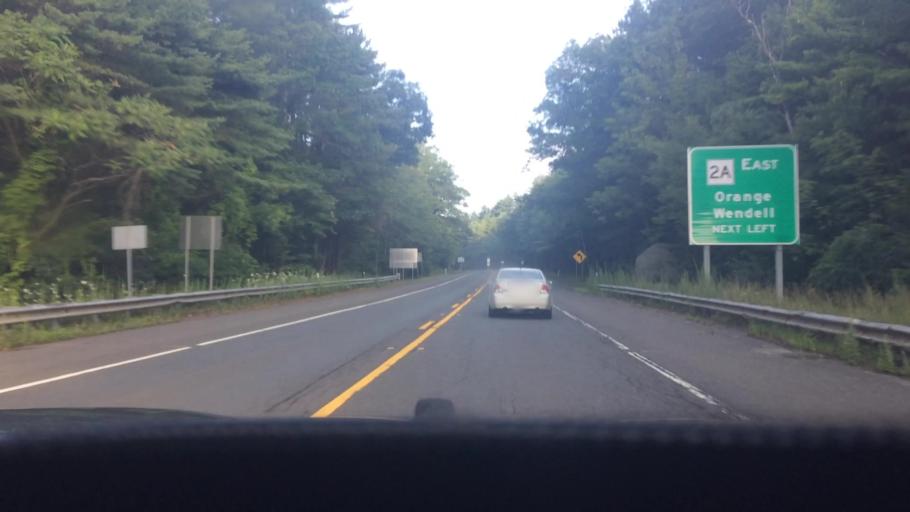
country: US
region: Massachusetts
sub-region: Franklin County
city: Erving
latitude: 42.5984
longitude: -72.3606
